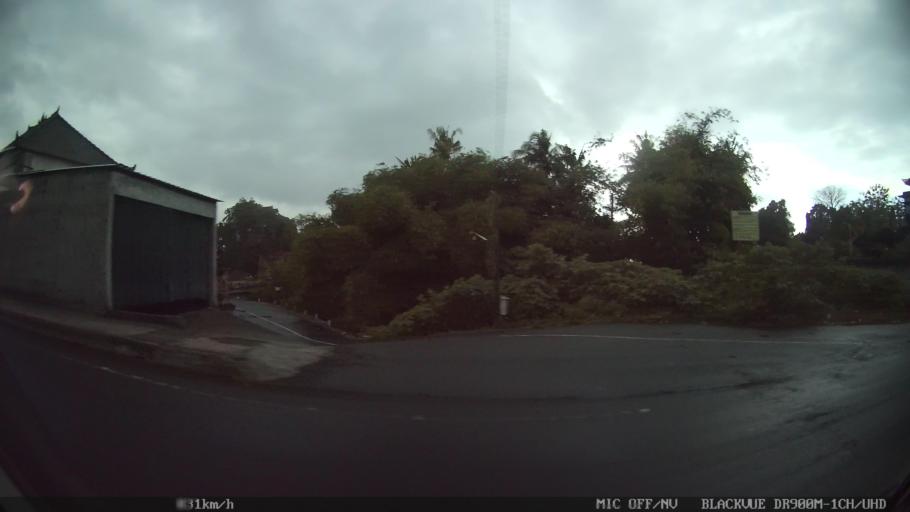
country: ID
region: Bali
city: Banjar Pasekan
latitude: -8.6048
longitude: 115.2832
